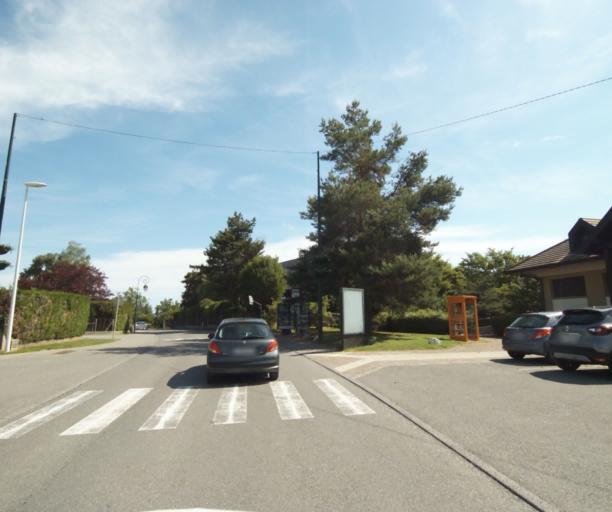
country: FR
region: Rhone-Alpes
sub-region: Departement de la Haute-Savoie
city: Margencel
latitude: 46.3385
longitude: 6.4328
